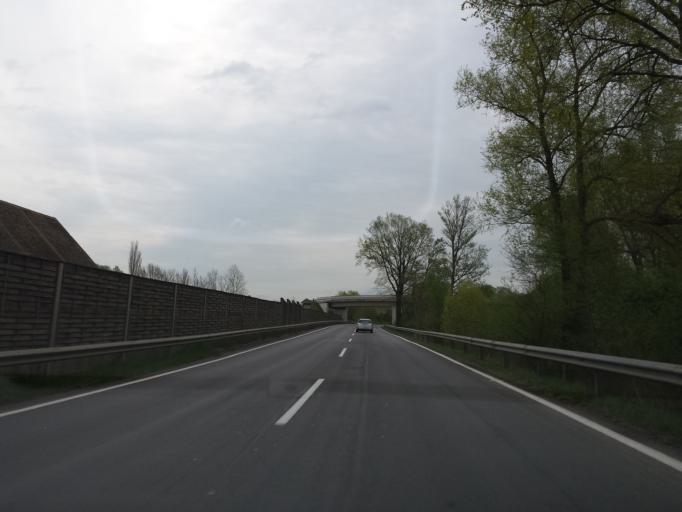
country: AT
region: Styria
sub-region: Politischer Bezirk Hartberg-Fuerstenfeld
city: Altenmarkt bei Fuerstenfeld
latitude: 47.0638
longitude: 16.0407
